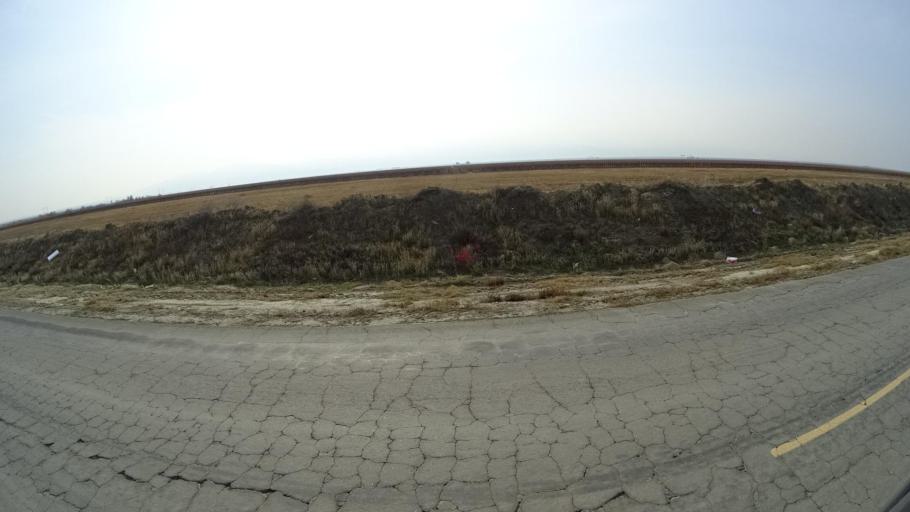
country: US
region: California
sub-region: Kern County
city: Greenfield
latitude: 35.0949
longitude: -119.0686
